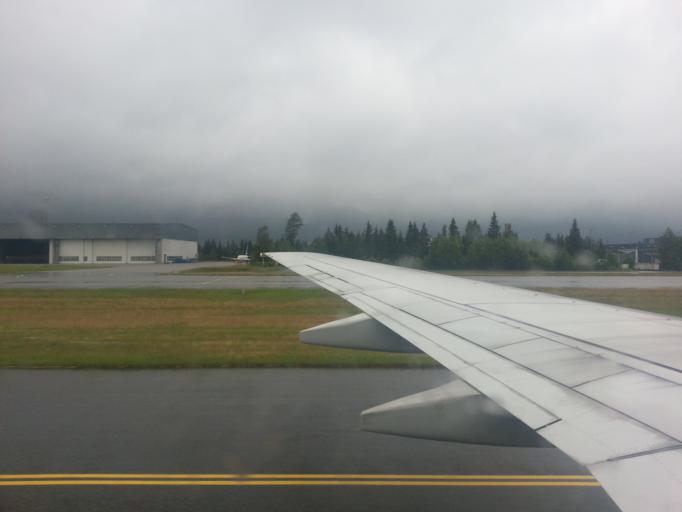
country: NO
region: Akershus
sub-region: Ullensaker
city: Jessheim
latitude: 60.1859
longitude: 11.1098
